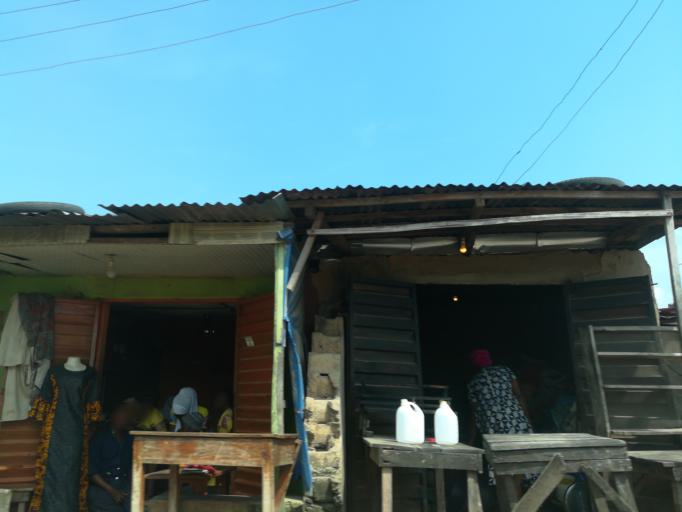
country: NG
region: Lagos
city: Ebute Ikorodu
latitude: 6.6251
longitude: 3.4824
